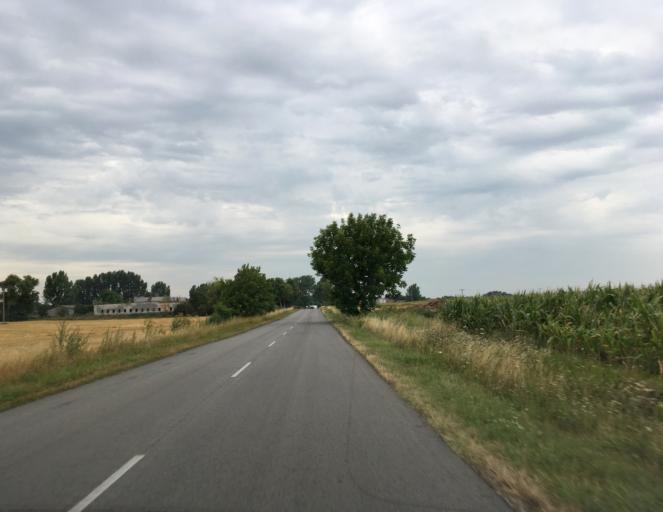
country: SK
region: Trnavsky
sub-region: Okres Dunajska Streda
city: Velky Meder
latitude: 47.9266
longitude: 17.7002
